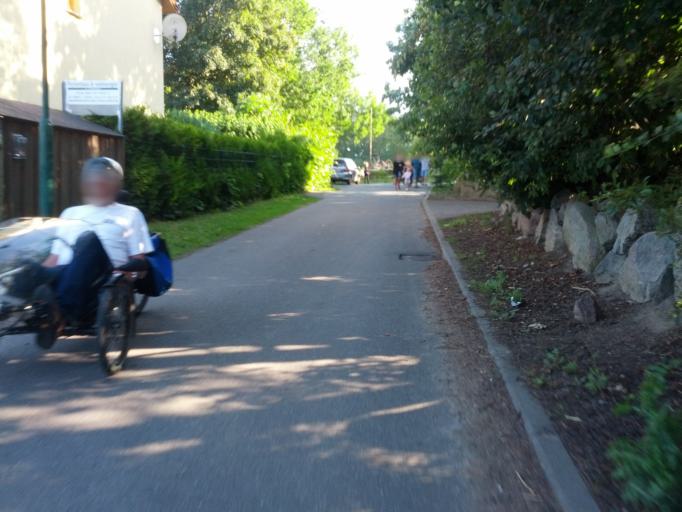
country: DE
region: Mecklenburg-Vorpommern
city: Bastorf
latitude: 54.1384
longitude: 11.6792
